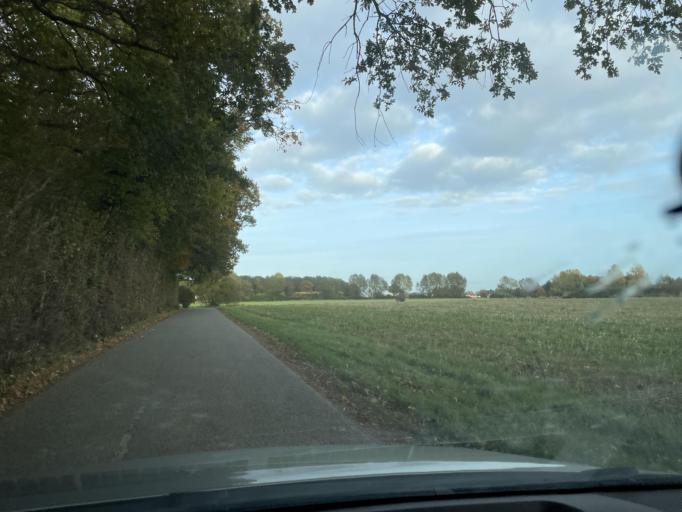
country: DK
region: South Denmark
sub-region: Kerteminde Kommune
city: Kerteminde
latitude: 55.4206
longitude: 10.6822
